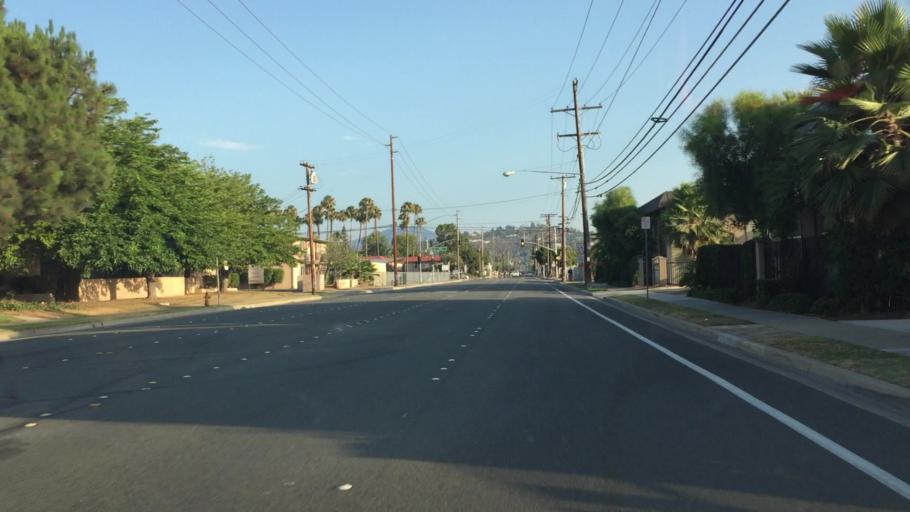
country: US
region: California
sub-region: San Diego County
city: El Cajon
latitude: 32.7995
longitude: -116.9511
